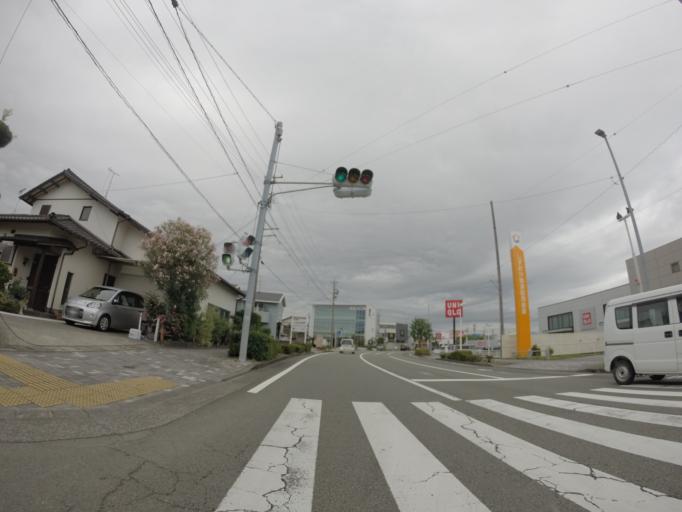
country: JP
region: Shizuoka
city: Yaizu
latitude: 34.8613
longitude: 138.3082
